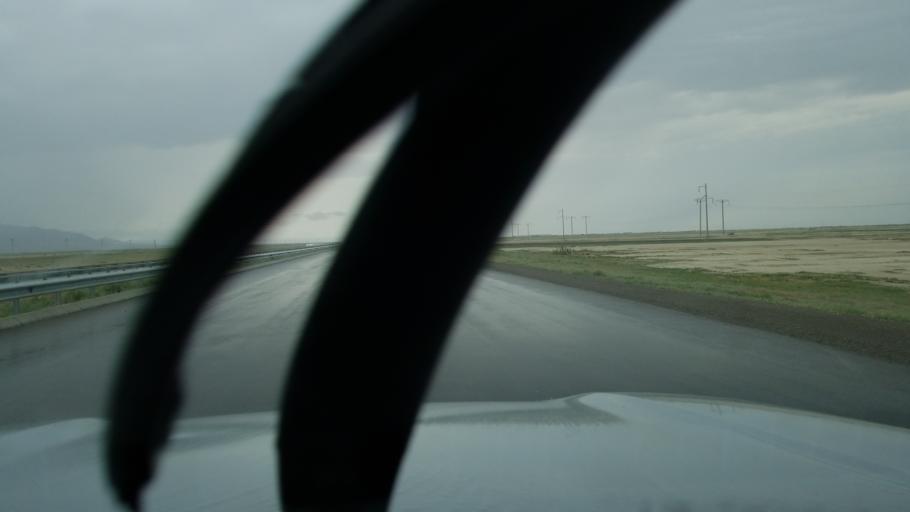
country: TM
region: Balkan
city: Serdar
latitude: 39.0316
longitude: 56.1791
